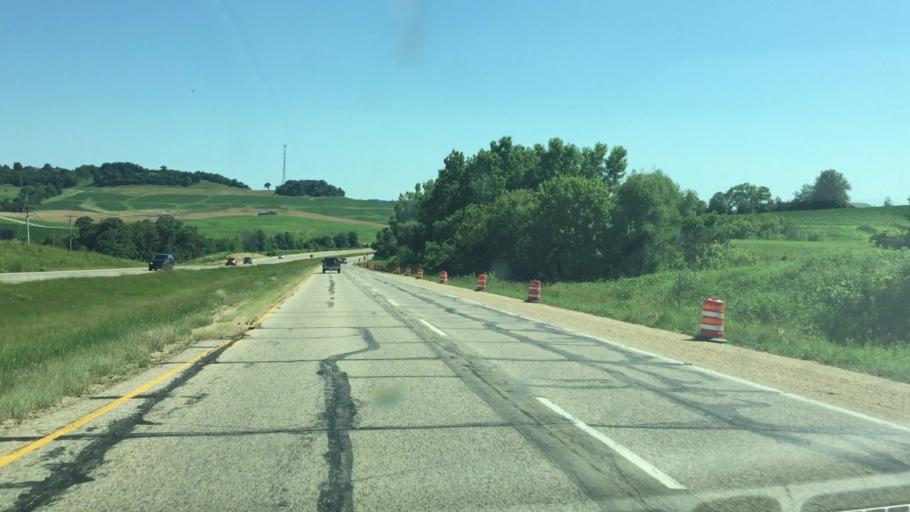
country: US
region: Iowa
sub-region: Dubuque County
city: Dubuque
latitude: 42.4417
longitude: -90.6802
